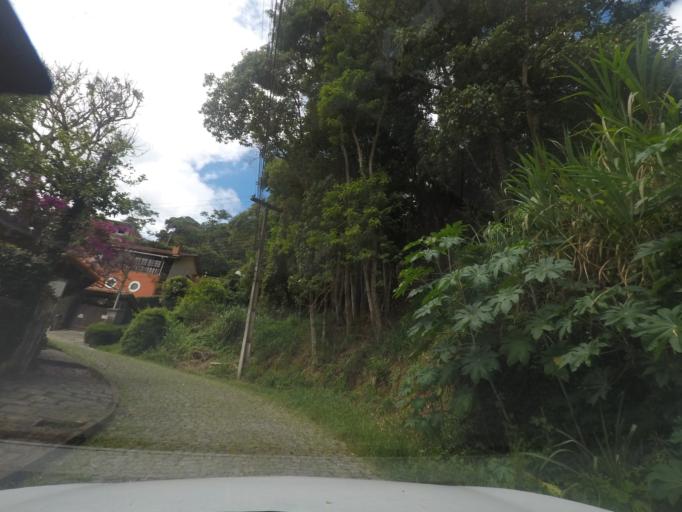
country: BR
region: Rio de Janeiro
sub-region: Teresopolis
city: Teresopolis
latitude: -22.3991
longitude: -42.9858
